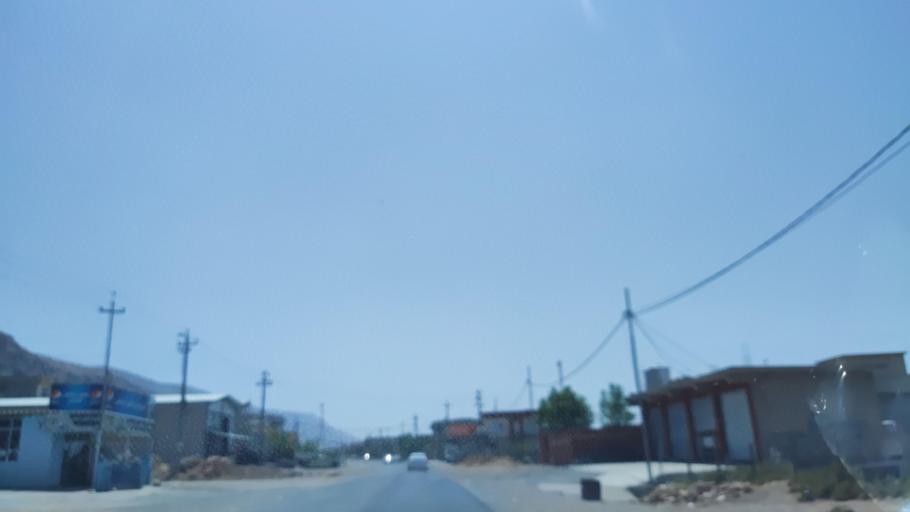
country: IQ
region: Arbil
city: Shaqlawah
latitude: 36.5702
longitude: 44.3338
